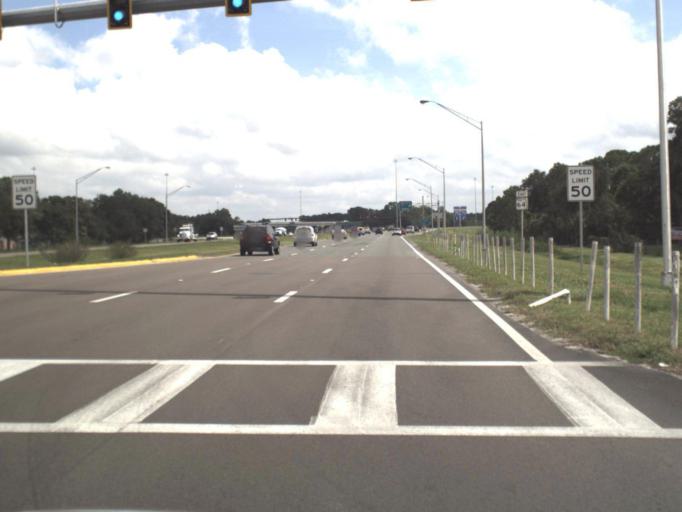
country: US
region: Florida
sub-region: Manatee County
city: Ellenton
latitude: 27.4920
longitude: -82.4789
